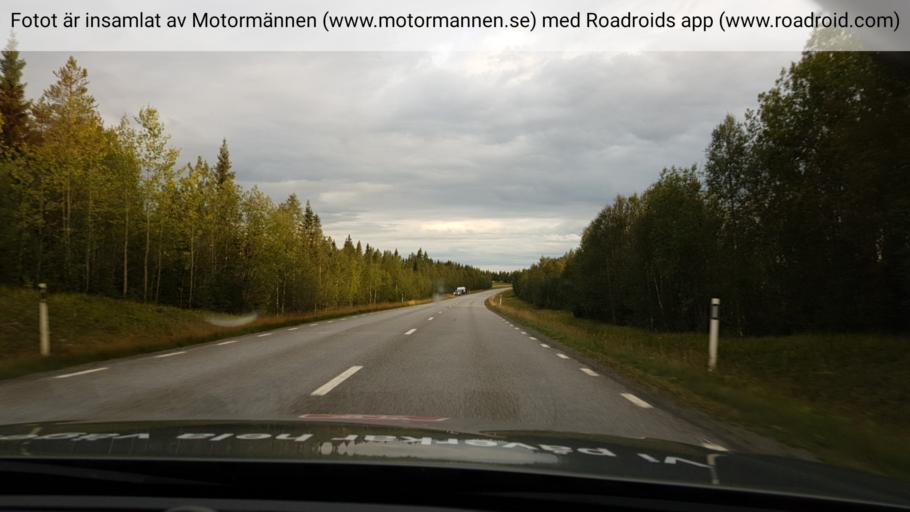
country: SE
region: Jaemtland
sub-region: OEstersunds Kommun
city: Lit
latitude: 63.4303
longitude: 15.1200
